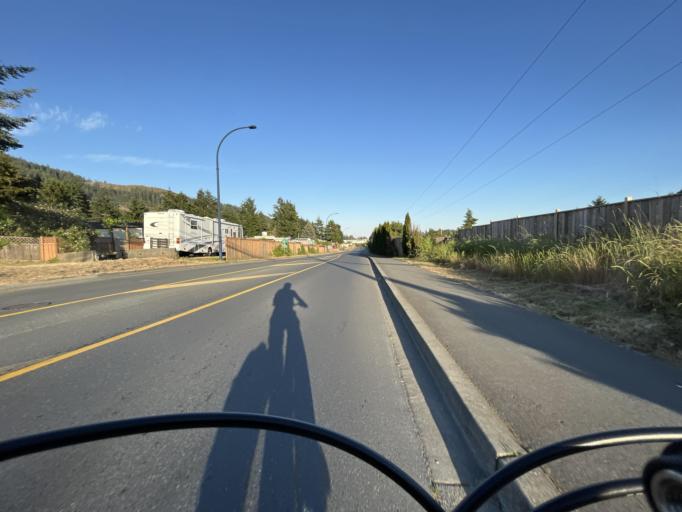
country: CA
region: British Columbia
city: Langford
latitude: 48.4600
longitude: -123.5483
